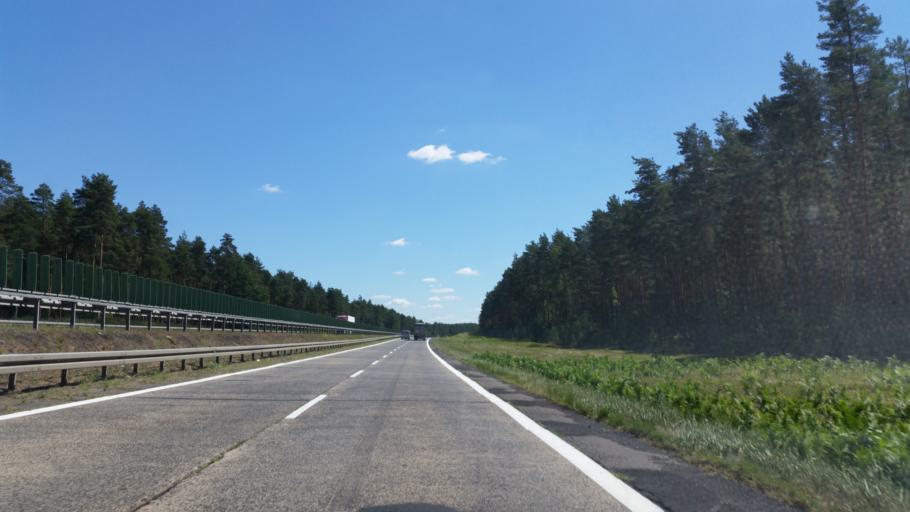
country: PL
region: Lubusz
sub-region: Powiat zaganski
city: Malomice
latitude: 51.4181
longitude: 15.4789
